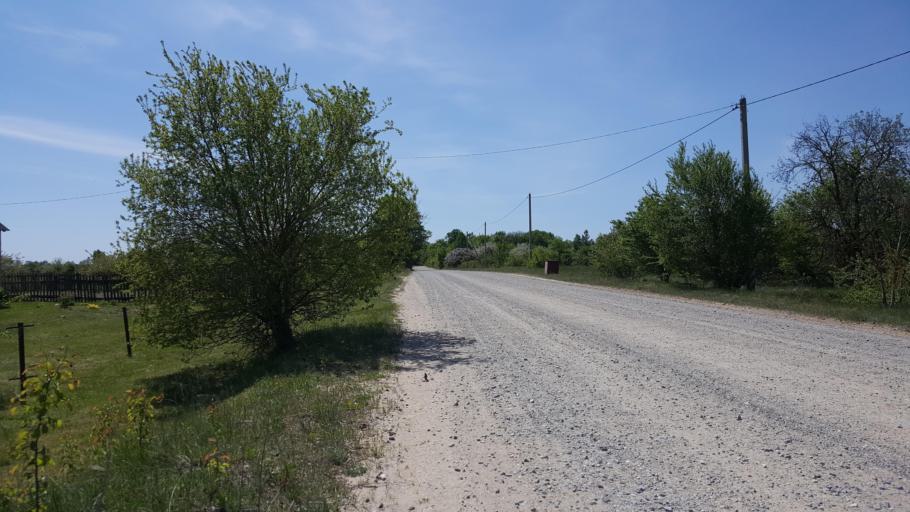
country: BY
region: Brest
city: Zhabinka
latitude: 52.3581
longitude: 24.1560
